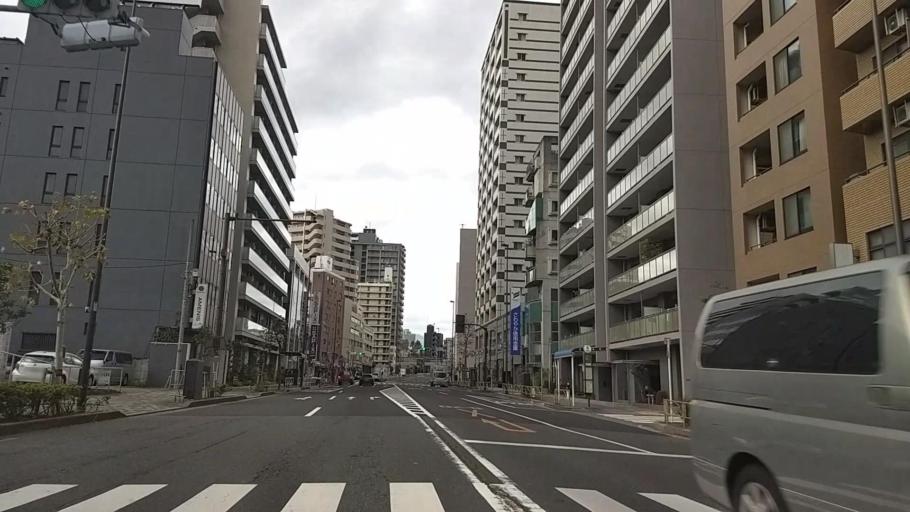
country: JP
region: Tokyo
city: Tokyo
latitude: 35.6446
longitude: 139.7376
